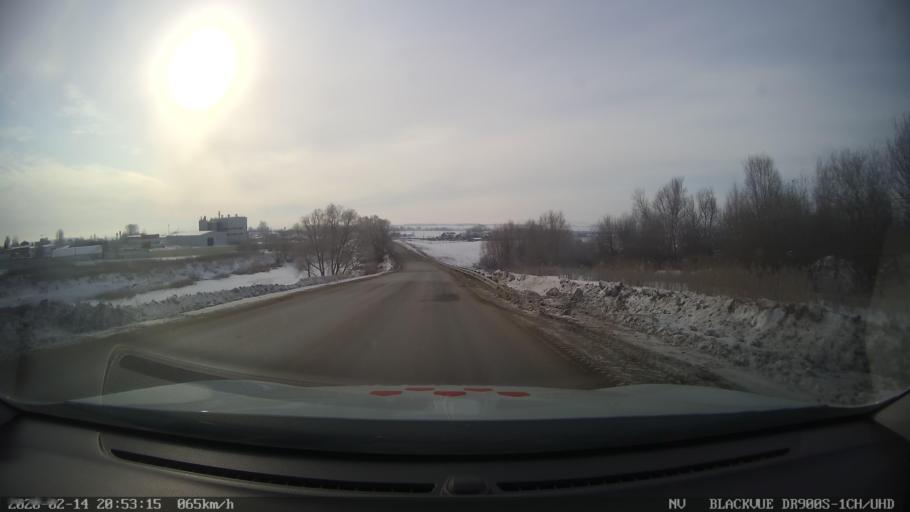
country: RU
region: Tatarstan
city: Kuybyshevskiy Zaton
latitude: 55.1965
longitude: 49.2477
